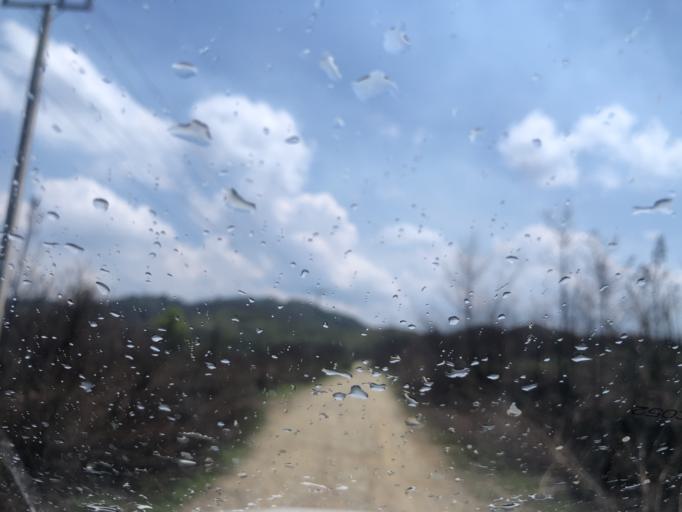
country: LA
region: Phongsali
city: Phongsali
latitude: 21.4082
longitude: 102.1863
